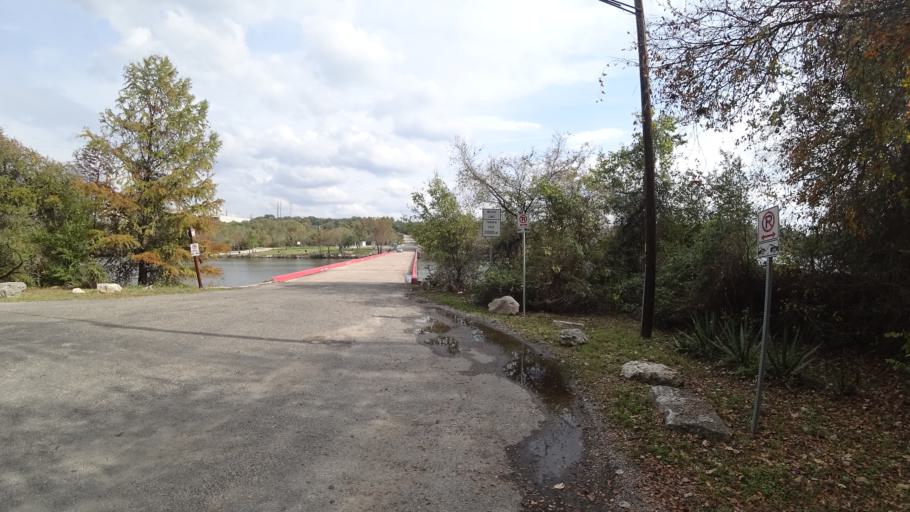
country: US
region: Texas
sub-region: Travis County
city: Hudson Bend
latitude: 30.3885
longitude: -97.9140
